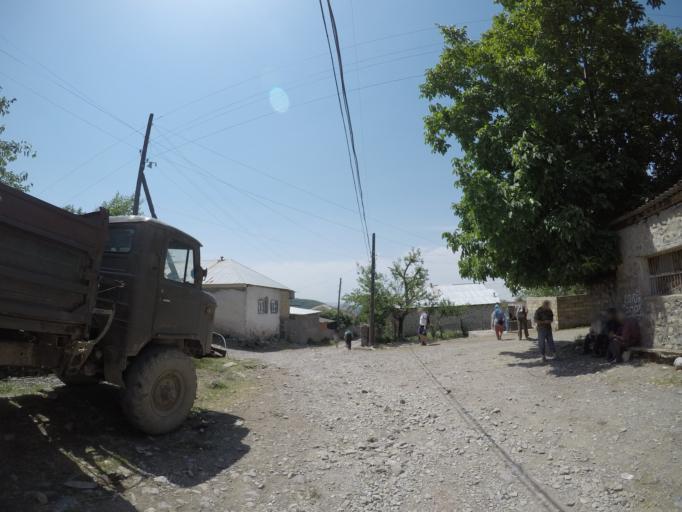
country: AZ
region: Qakh Rayon
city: Cinarli
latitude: 41.4852
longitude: 46.8502
